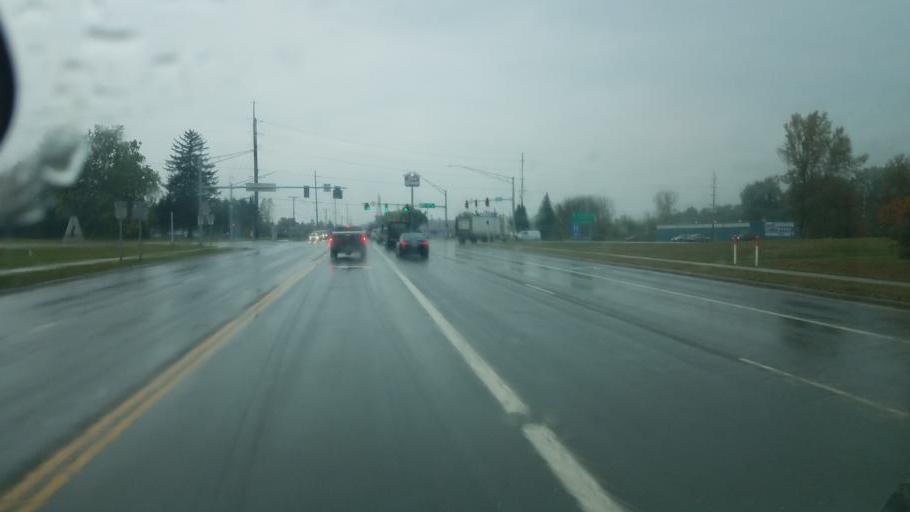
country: US
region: Ohio
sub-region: Ashland County
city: Ashland
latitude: 40.8631
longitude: -82.2868
